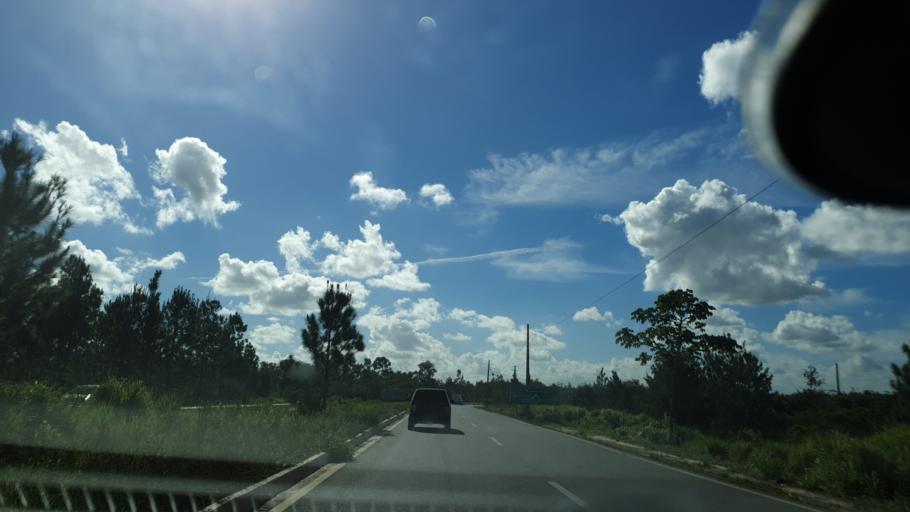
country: BR
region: Bahia
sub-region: Camacari
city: Camacari
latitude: -12.6825
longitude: -38.2999
